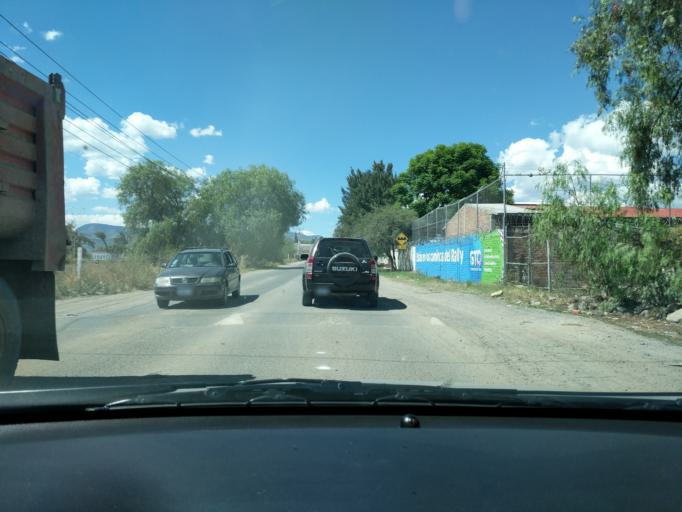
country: MX
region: Guanajuato
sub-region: Leon
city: Ladrilleras del Refugio
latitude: 21.0701
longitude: -101.5502
